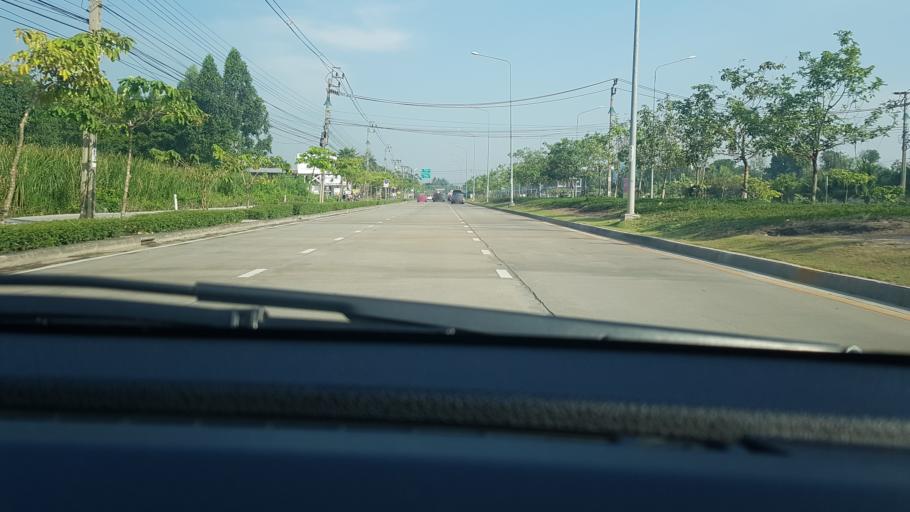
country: TH
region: Bangkok
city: Thawi Watthana
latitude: 13.7967
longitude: 100.3637
